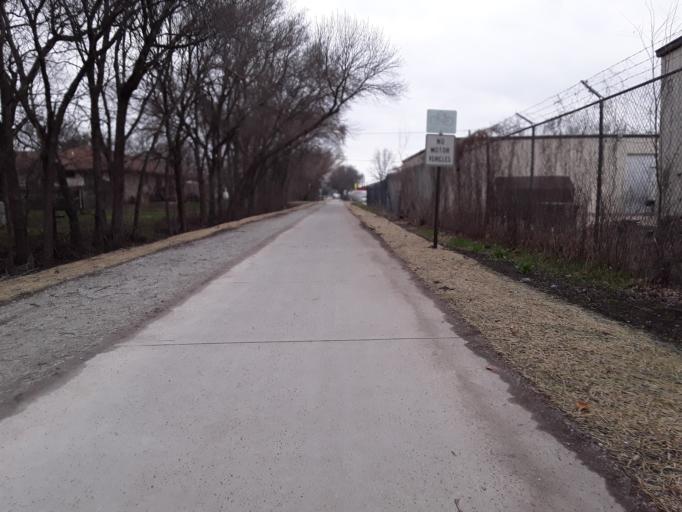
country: US
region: Nebraska
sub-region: Lancaster County
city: Lincoln
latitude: 40.8514
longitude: -96.6332
